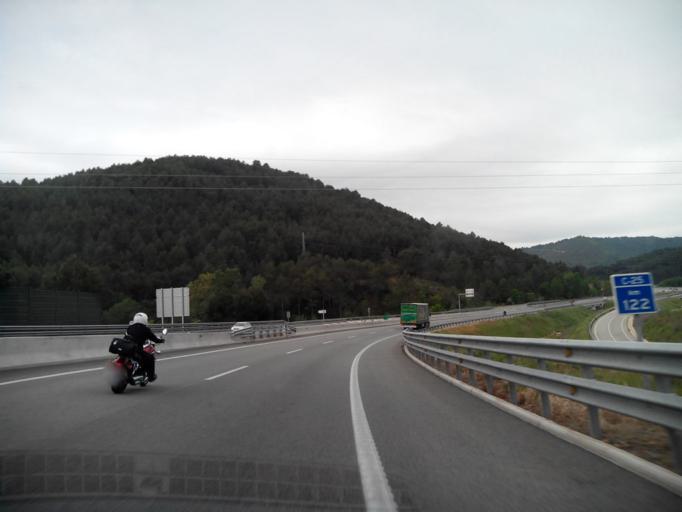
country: ES
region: Catalonia
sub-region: Provincia de Barcelona
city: Rajadell
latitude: 41.7341
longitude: 1.6955
